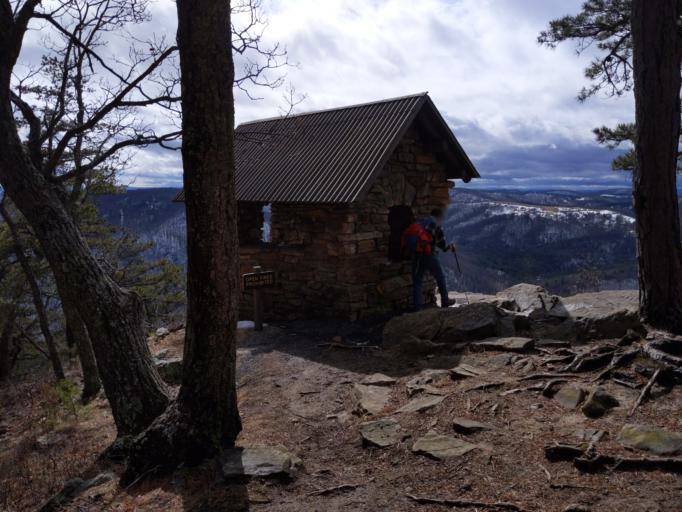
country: US
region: Virginia
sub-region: Shenandoah County
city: Basye
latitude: 38.9013
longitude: -78.9056
